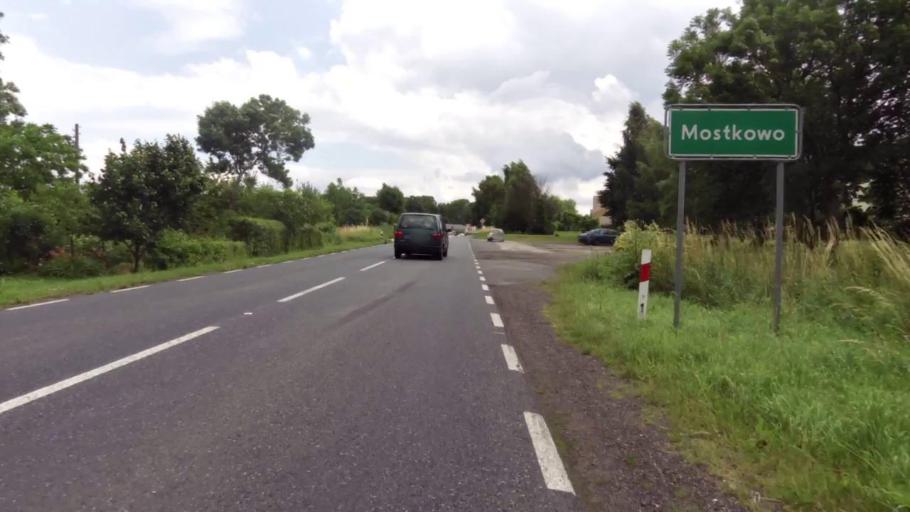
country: PL
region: West Pomeranian Voivodeship
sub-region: Powiat pyrzycki
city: Lipiany
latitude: 52.9952
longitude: 15.0500
